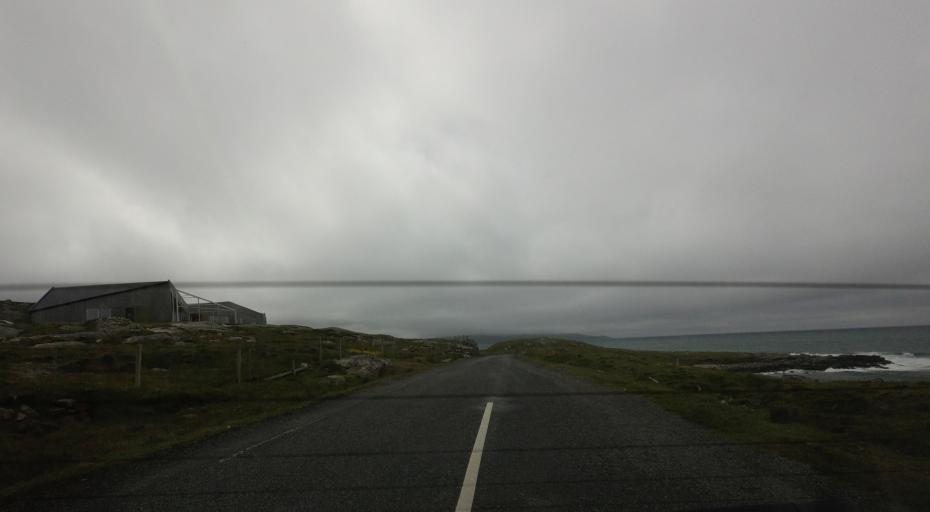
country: GB
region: Scotland
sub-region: Eilean Siar
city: Harris
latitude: 57.8582
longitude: -6.9953
